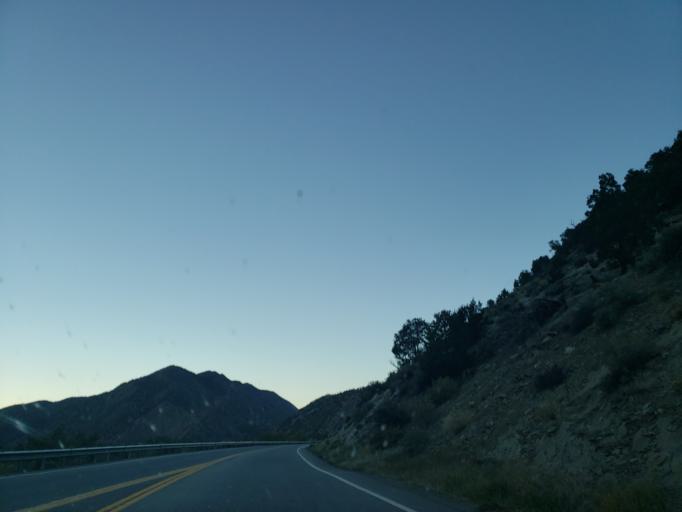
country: US
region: Colorado
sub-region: Garfield County
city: New Castle
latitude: 39.5690
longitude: -107.5197
